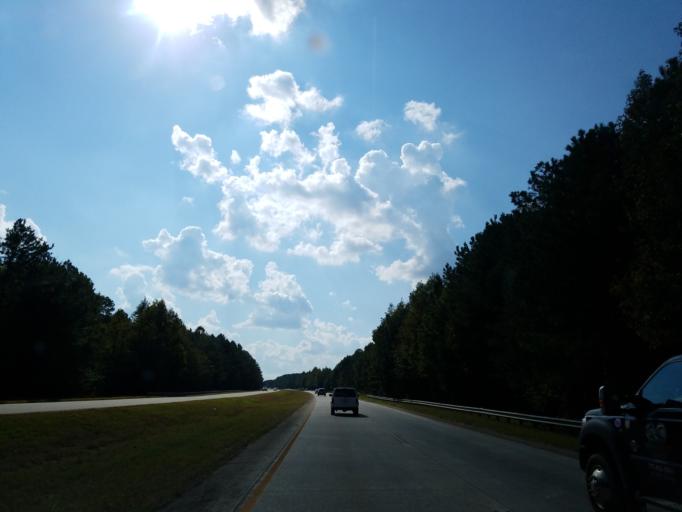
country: US
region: Georgia
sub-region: Barrow County
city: Statham
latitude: 33.9610
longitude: -83.6404
